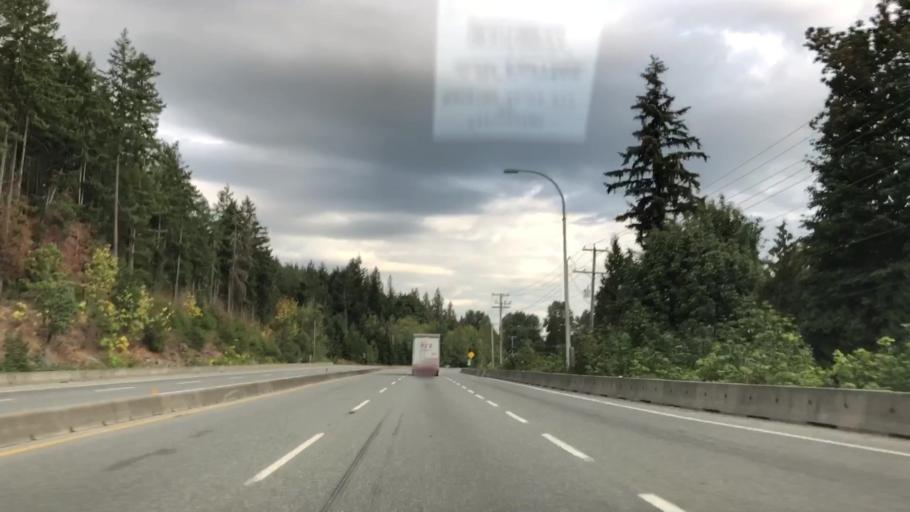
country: CA
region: British Columbia
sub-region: Cowichan Valley Regional District
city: Ladysmith
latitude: 49.0267
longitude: -123.8621
